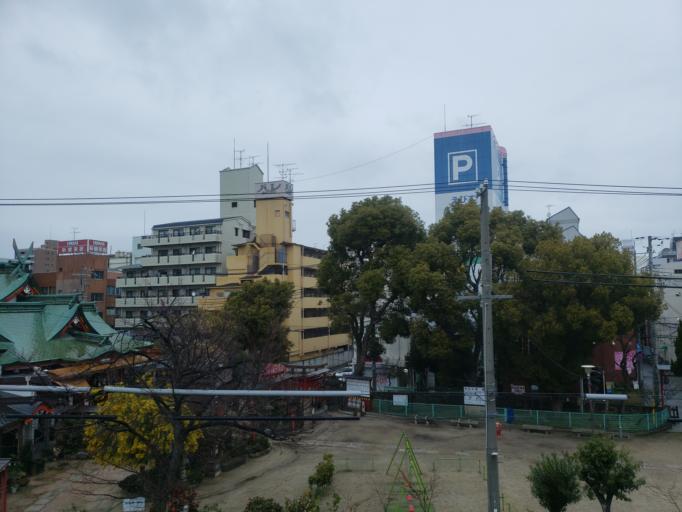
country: JP
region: Hyogo
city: Amagasaki
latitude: 34.7194
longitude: 135.4130
